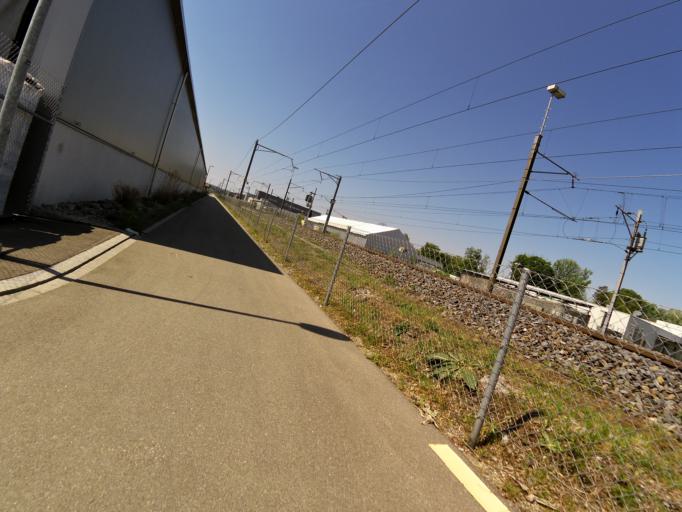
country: CH
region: Thurgau
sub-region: Frauenfeld District
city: Frauenfeld
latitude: 47.5695
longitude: 8.9170
